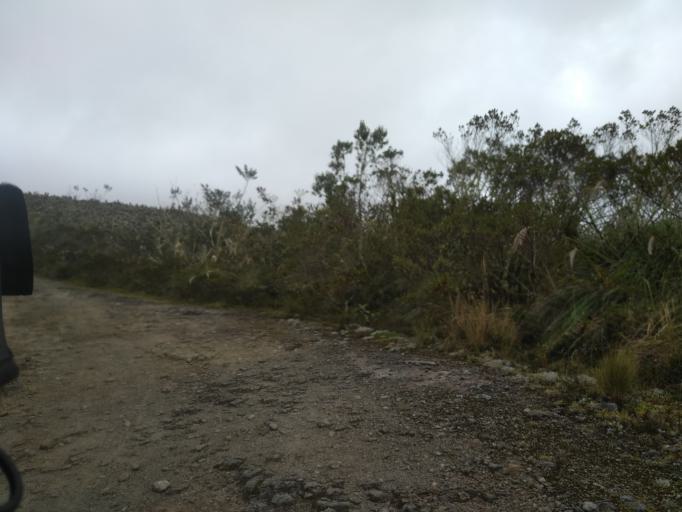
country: EC
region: Carchi
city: San Gabriel
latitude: 0.7063
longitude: -77.8302
